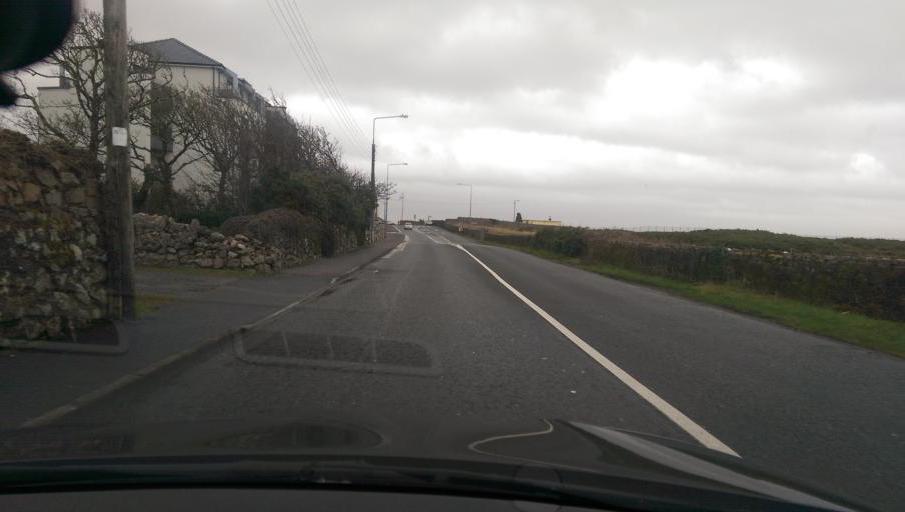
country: IE
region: Connaught
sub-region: County Galway
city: Gaillimh
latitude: 53.2580
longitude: -9.0951
